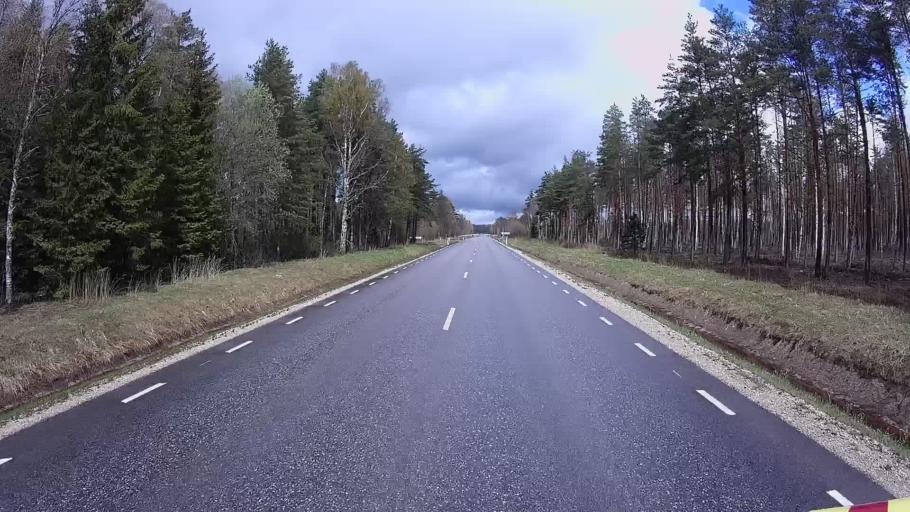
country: EE
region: Hiiumaa
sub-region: Kaerdla linn
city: Kardla
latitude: 58.8672
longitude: 22.7843
